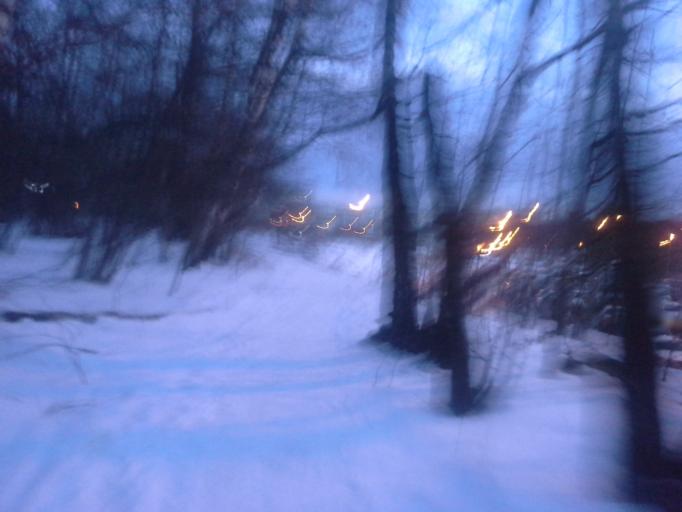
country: RU
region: Moscow
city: Chertanovo Yuzhnoye
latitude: 55.5665
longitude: 37.5548
